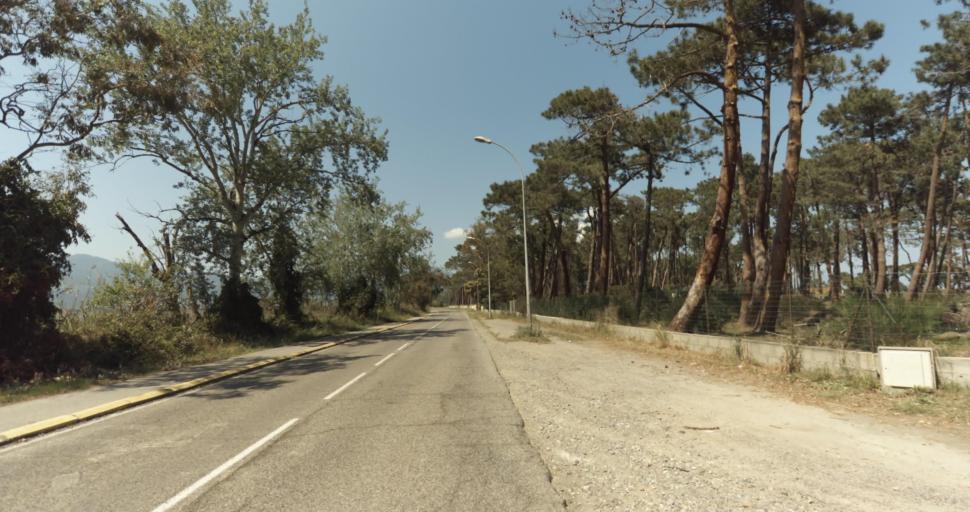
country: FR
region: Corsica
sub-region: Departement de la Haute-Corse
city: Biguglia
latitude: 42.6182
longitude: 9.4764
